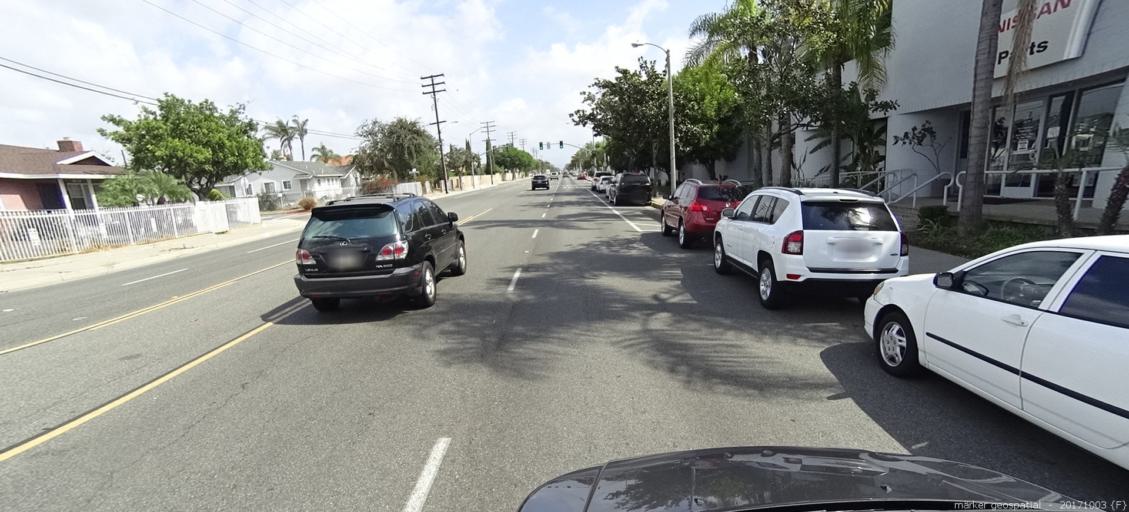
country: US
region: California
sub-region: Orange County
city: Garden Grove
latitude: 33.7666
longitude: -117.9670
